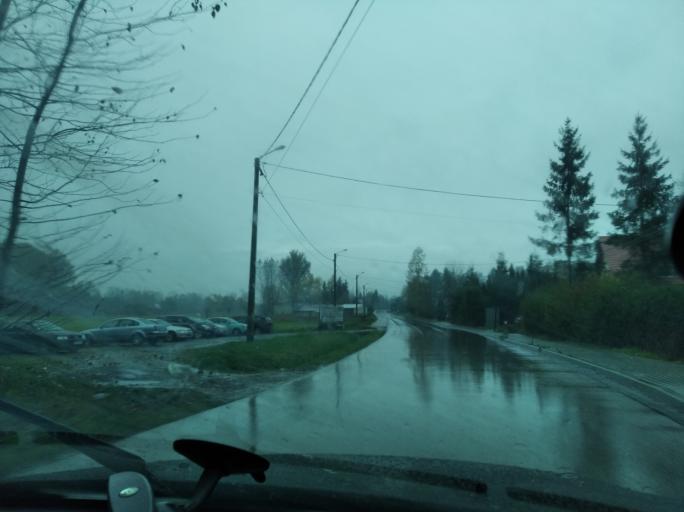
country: PL
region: Subcarpathian Voivodeship
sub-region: Powiat lancucki
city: Albigowa
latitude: 50.0383
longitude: 22.2043
